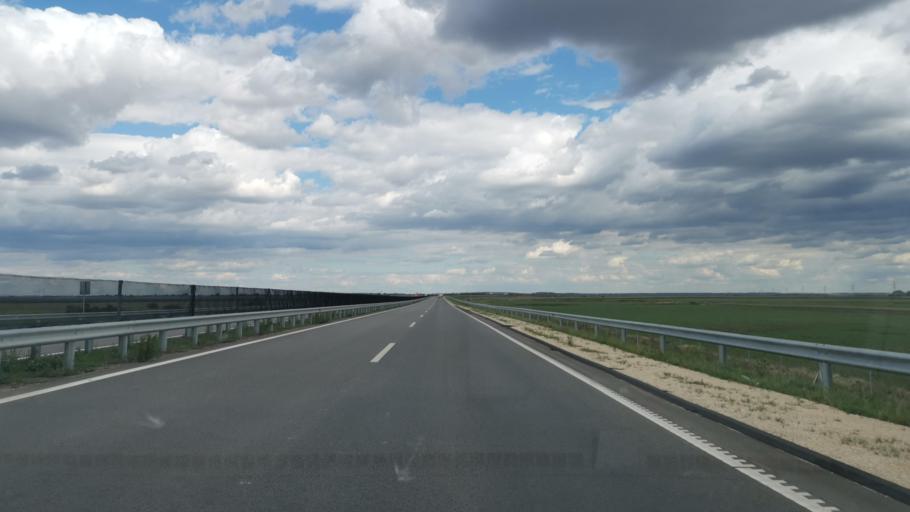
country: HU
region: Jasz-Nagykun-Szolnok
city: Zagyvarekas
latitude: 47.2204
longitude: 20.1599
